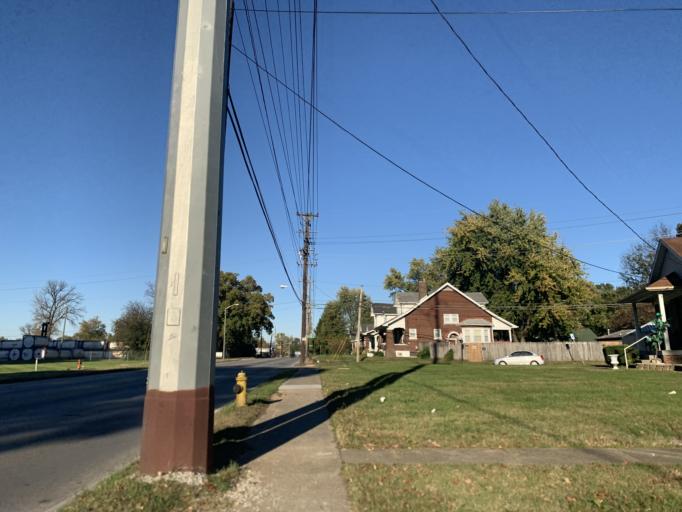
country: US
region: Kentucky
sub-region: Jefferson County
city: Shively
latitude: 38.2160
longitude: -85.7817
